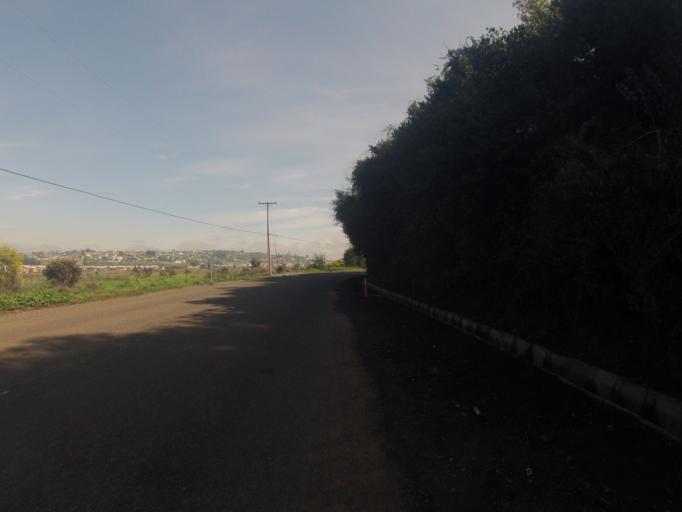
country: CL
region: Araucania
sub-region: Provincia de Cautin
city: Temuco
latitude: -38.7245
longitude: -72.6009
